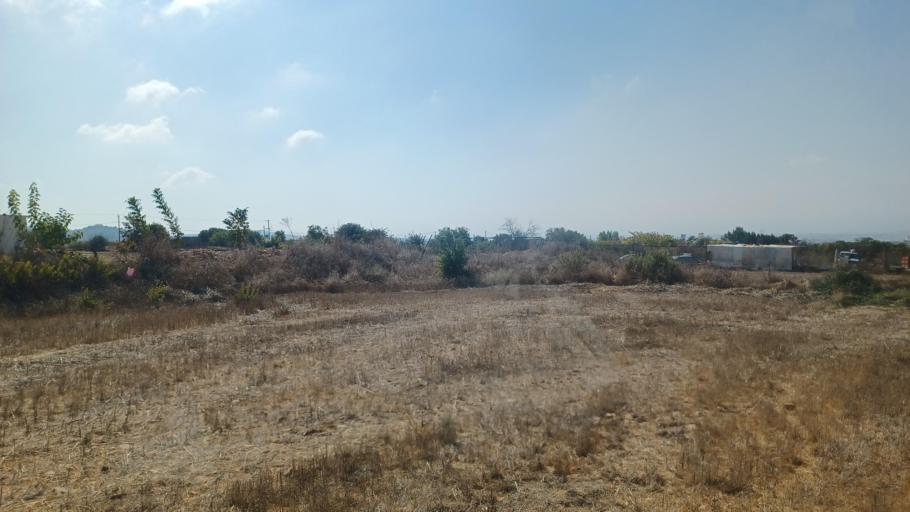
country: CY
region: Pafos
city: Mesogi
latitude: 34.8285
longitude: 32.4506
